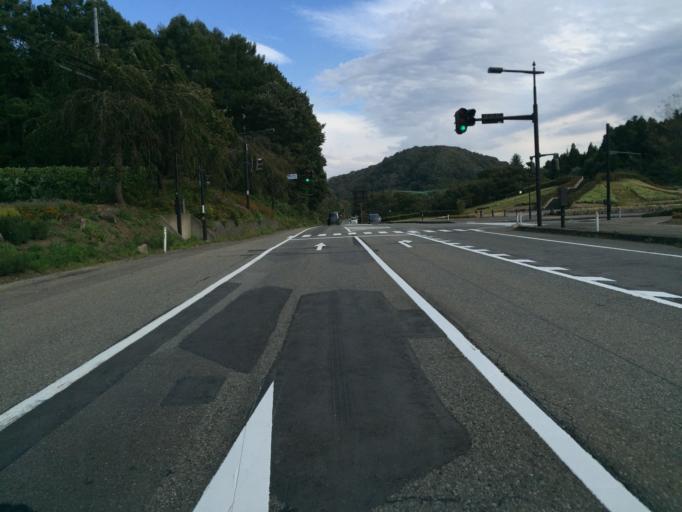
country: JP
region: Fukushima
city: Inawashiro
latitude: 37.5192
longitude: 140.0176
